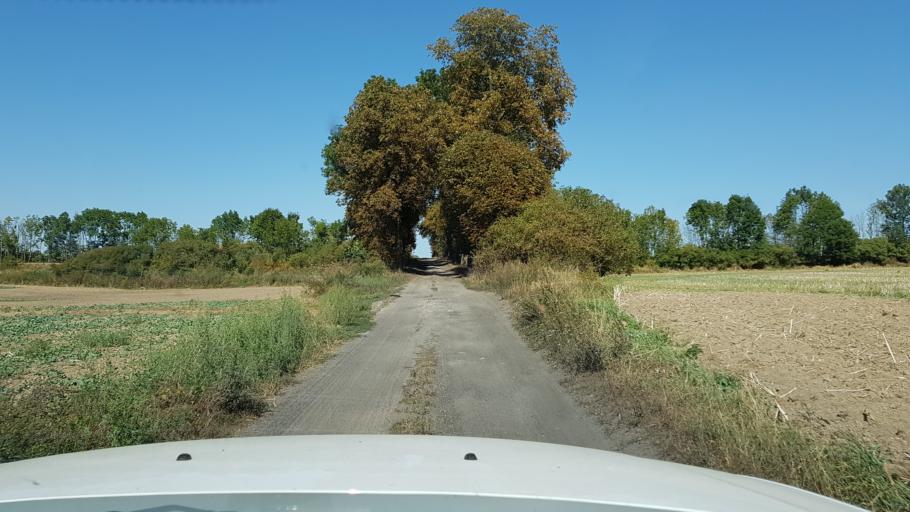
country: PL
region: West Pomeranian Voivodeship
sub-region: Powiat gryfinski
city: Moryn
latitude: 52.8630
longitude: 14.3552
